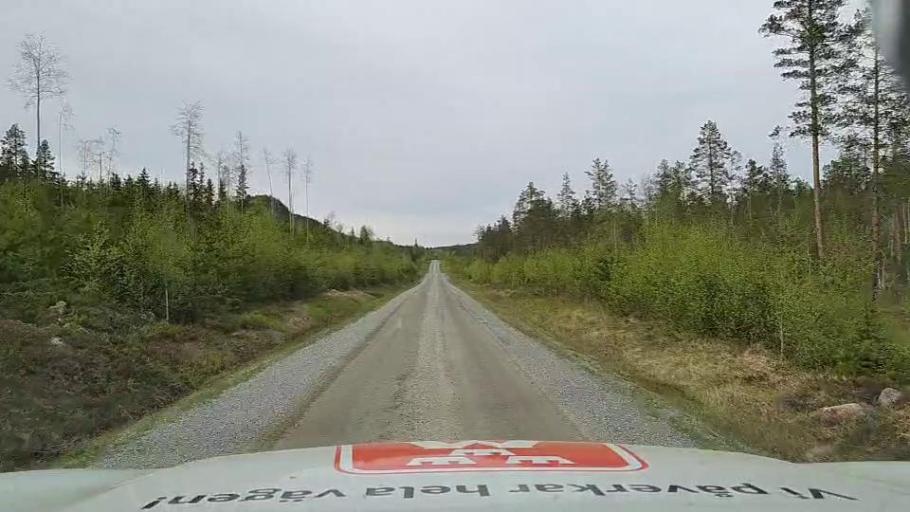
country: SE
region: Jaemtland
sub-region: Bergs Kommun
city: Hoverberg
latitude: 62.5516
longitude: 14.8977
